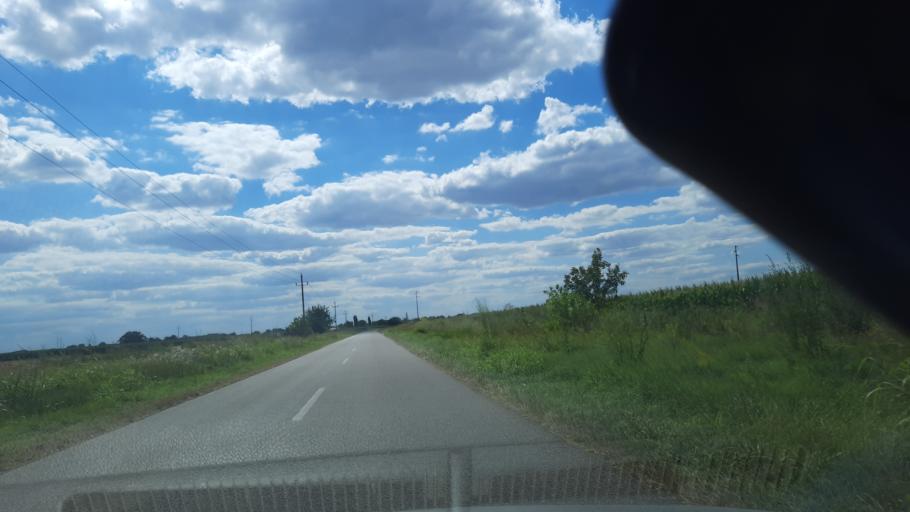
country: RS
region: Autonomna Pokrajina Vojvodina
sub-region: Sremski Okrug
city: Pecinci
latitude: 44.9070
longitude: 19.9482
